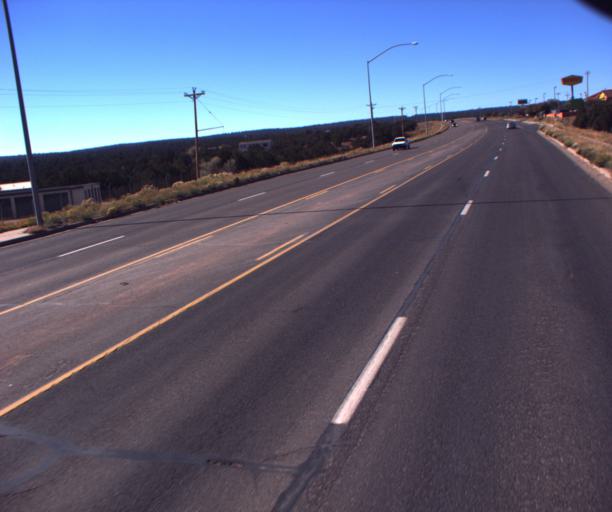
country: US
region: Arizona
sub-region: Apache County
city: Saint Michaels
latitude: 35.6576
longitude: -109.1113
